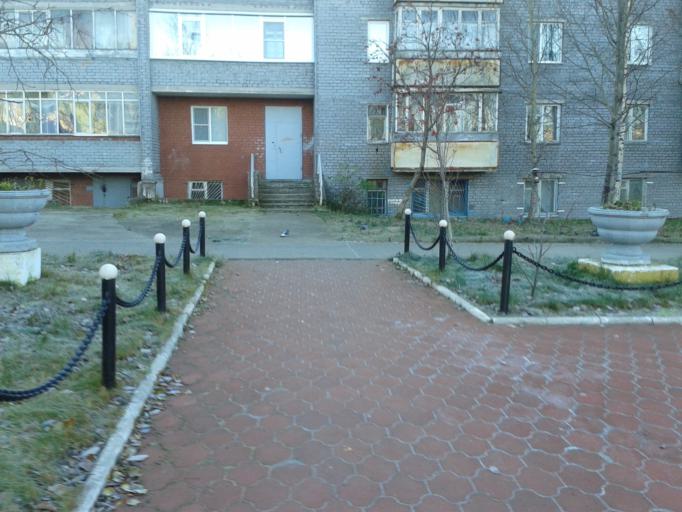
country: RU
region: Murmansk
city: Polyarnyye Zori
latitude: 67.3711
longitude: 32.4935
